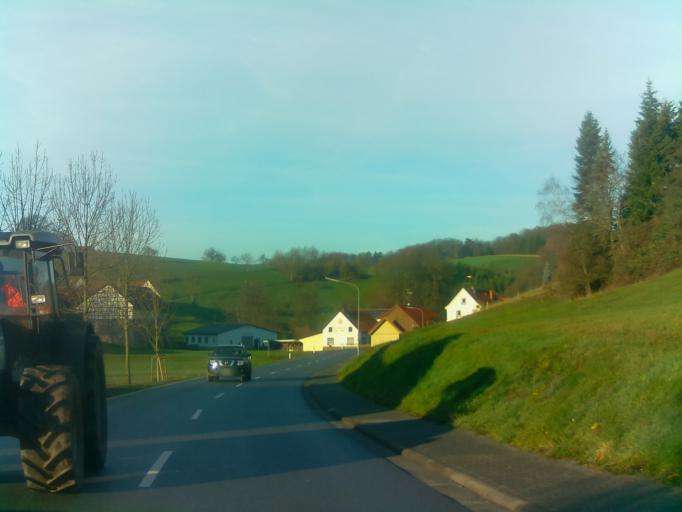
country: DE
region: Hesse
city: Reichelsheim
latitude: 49.6825
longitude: 8.8811
